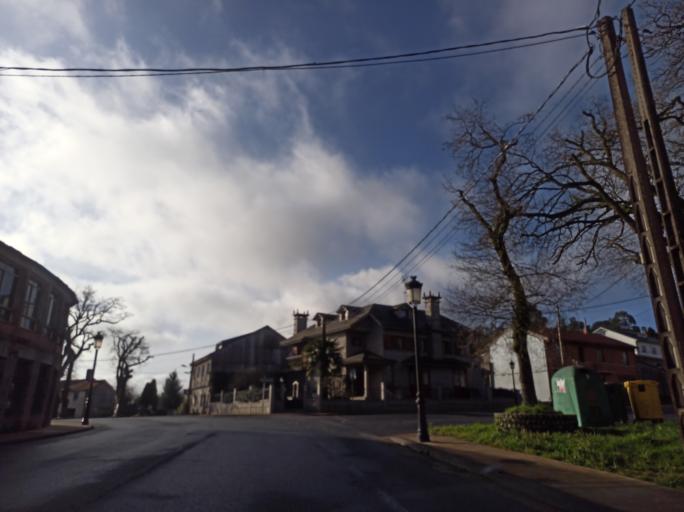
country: ES
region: Galicia
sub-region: Provincia da Coruna
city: Sobrado
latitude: 43.0785
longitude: -8.0133
